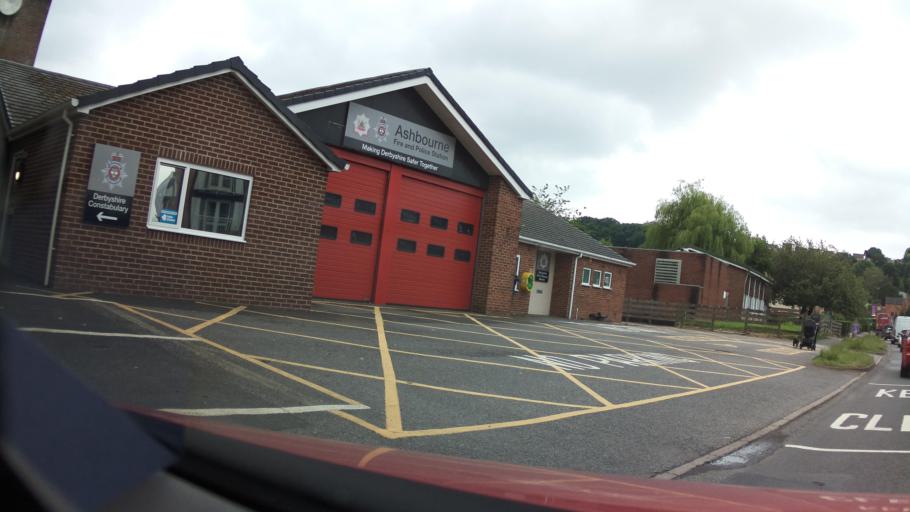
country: GB
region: England
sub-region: Derbyshire
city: Ashbourne
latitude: 53.0163
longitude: -1.7297
